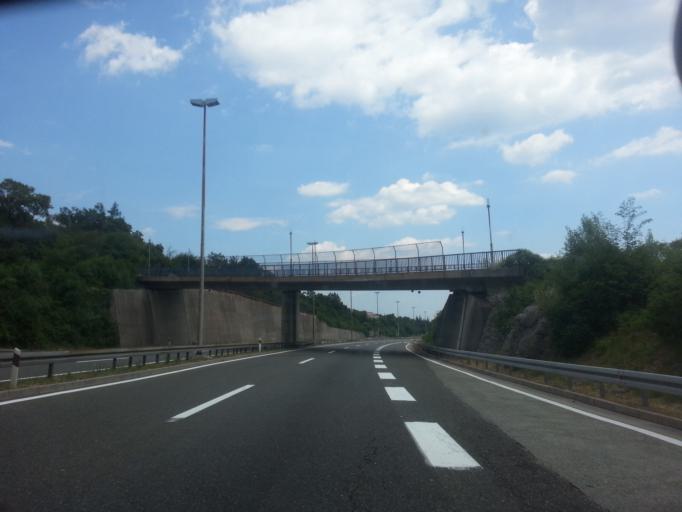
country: HR
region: Primorsko-Goranska
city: Rubesi
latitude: 45.3544
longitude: 14.3554
